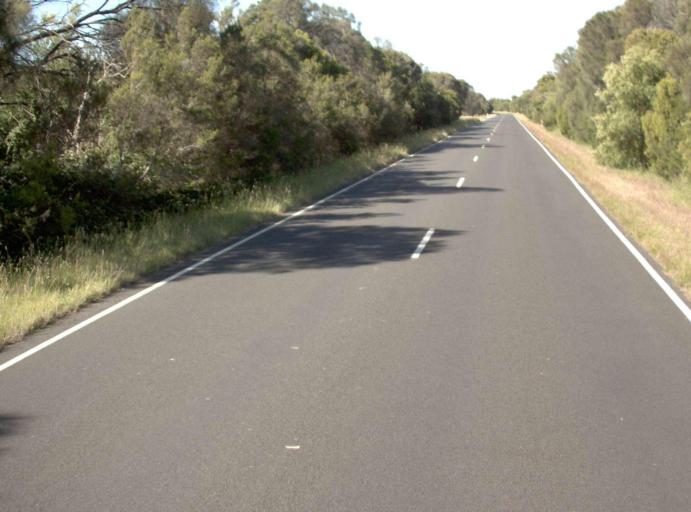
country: AU
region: Victoria
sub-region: Latrobe
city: Traralgon
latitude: -38.6377
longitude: 146.6733
